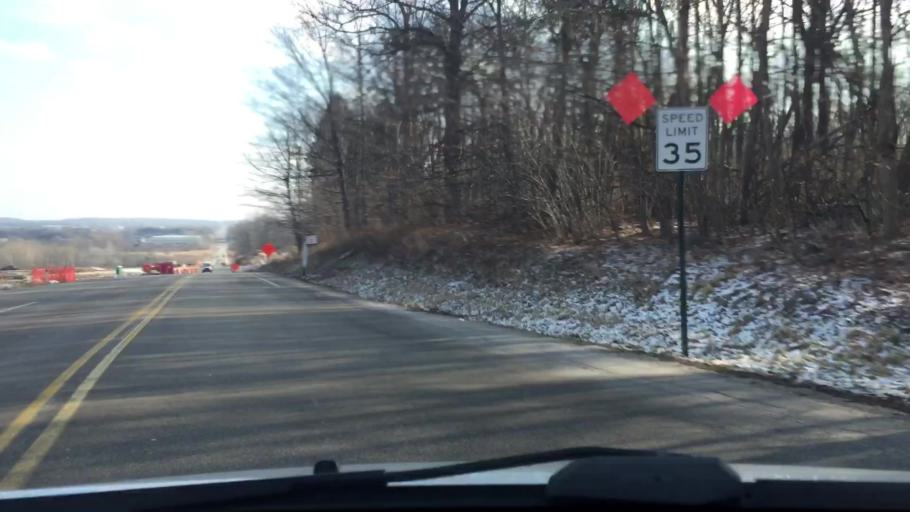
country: US
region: Wisconsin
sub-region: Waukesha County
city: Waukesha
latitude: 42.9886
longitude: -88.2886
